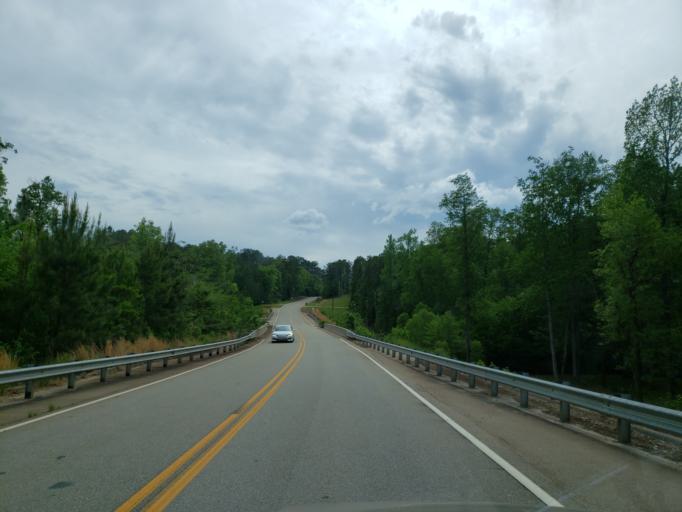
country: US
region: Georgia
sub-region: Monroe County
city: Forsyth
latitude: 32.9528
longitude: -83.9237
